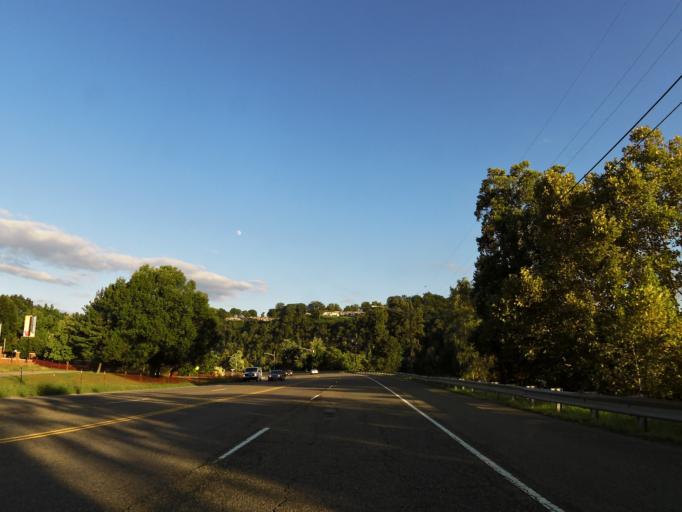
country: US
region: Tennessee
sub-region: Knox County
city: Knoxville
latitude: 35.9448
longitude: -83.9412
